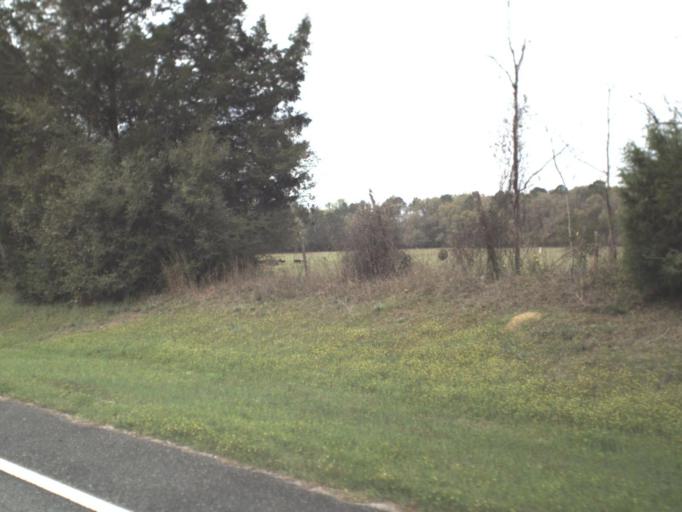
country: US
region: Florida
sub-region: Calhoun County
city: Blountstown
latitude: 30.5524
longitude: -85.1869
